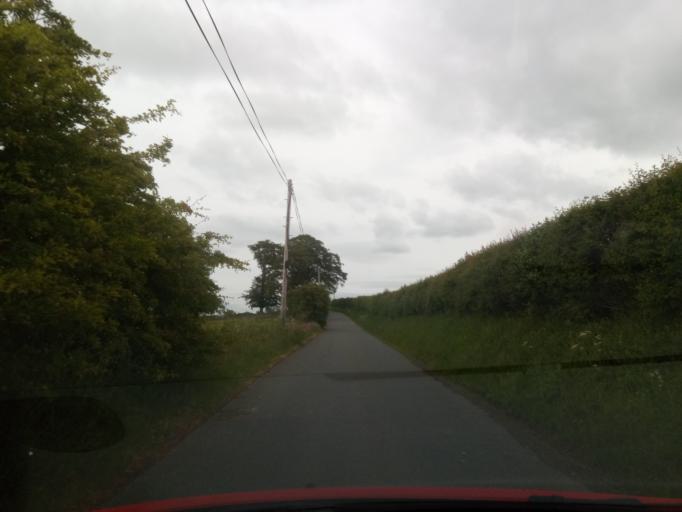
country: GB
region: Scotland
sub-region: The Scottish Borders
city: Selkirk
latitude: 55.5568
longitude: -2.8164
